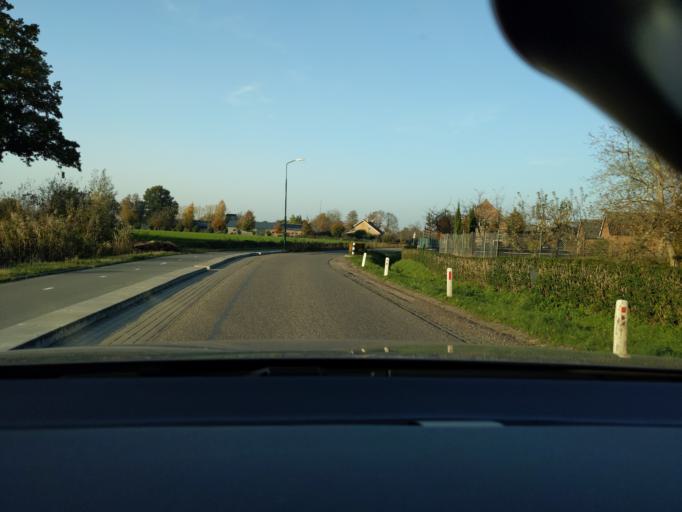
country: NL
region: North Brabant
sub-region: Gemeente Sint-Oedenrode
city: Sint-Oedenrode
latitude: 51.5671
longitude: 5.4306
